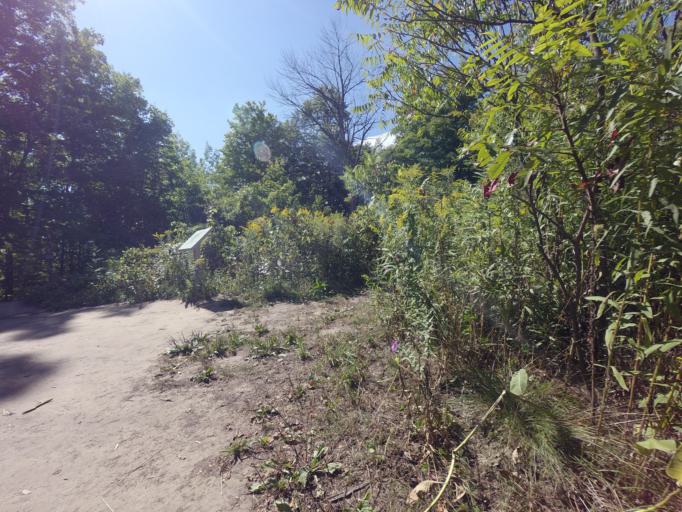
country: CA
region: Ontario
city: Orangeville
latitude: 43.8175
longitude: -80.0149
